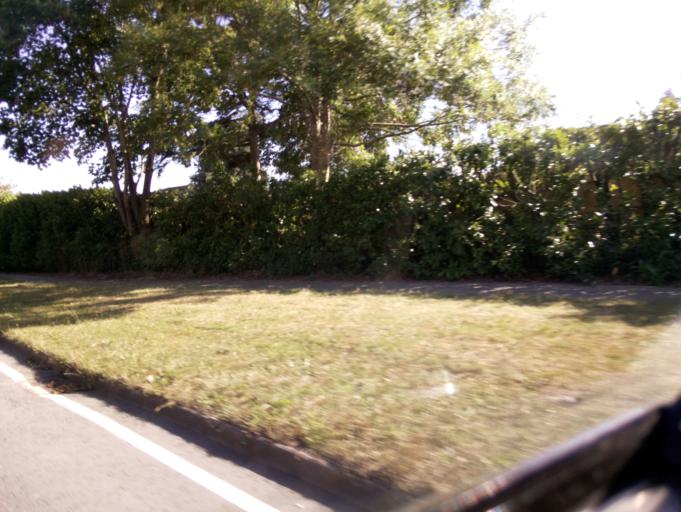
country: GB
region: England
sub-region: Dorset
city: Ferndown
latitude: 50.7888
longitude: -1.8827
